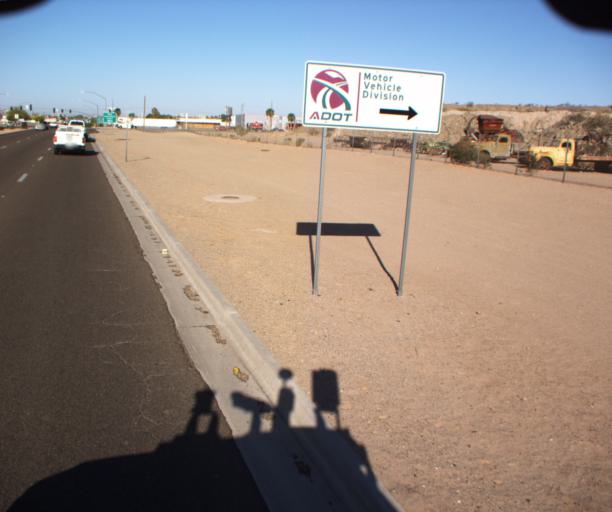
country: US
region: Arizona
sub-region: Yuma County
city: Yuma
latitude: 32.6696
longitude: -114.5961
